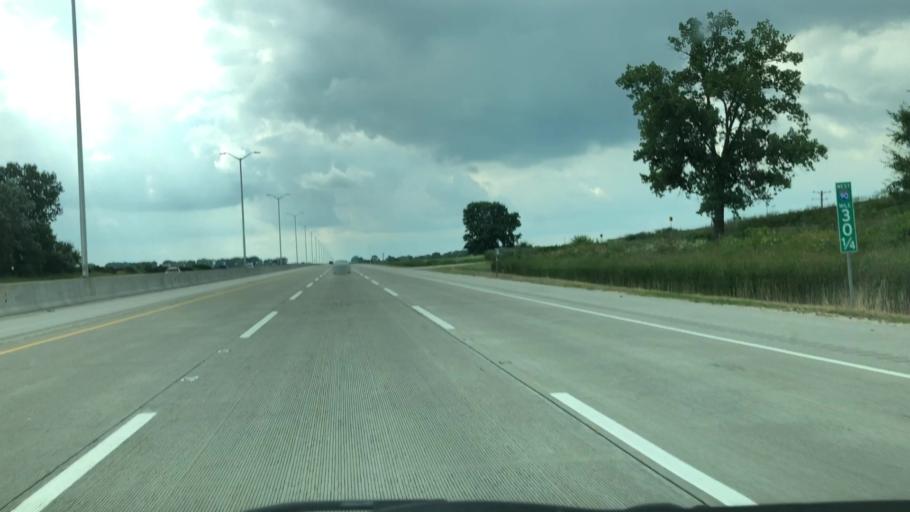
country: US
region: Illinois
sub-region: DeKalb County
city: Kingston
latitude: 42.2119
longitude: -88.7229
